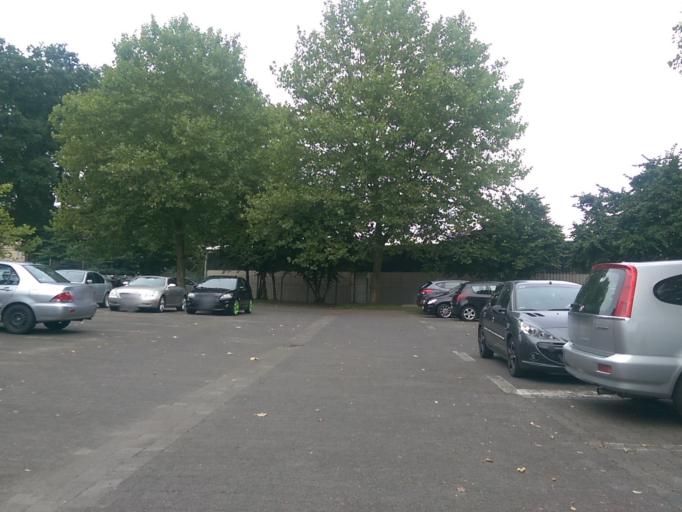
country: DE
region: North Rhine-Westphalia
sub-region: Regierungsbezirk Detmold
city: Guetersloh
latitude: 51.8963
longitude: 8.3722
